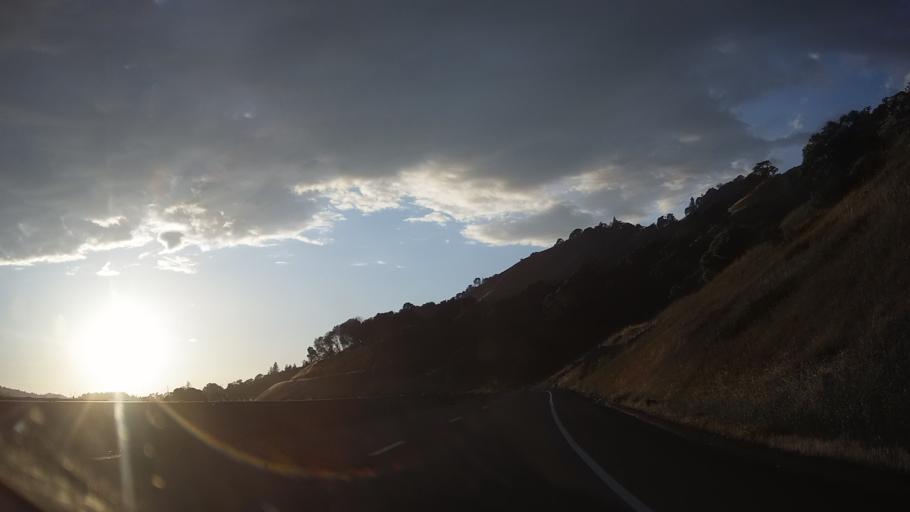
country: US
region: California
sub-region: Mendocino County
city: Redwood Valley
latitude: 39.2948
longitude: -123.2776
